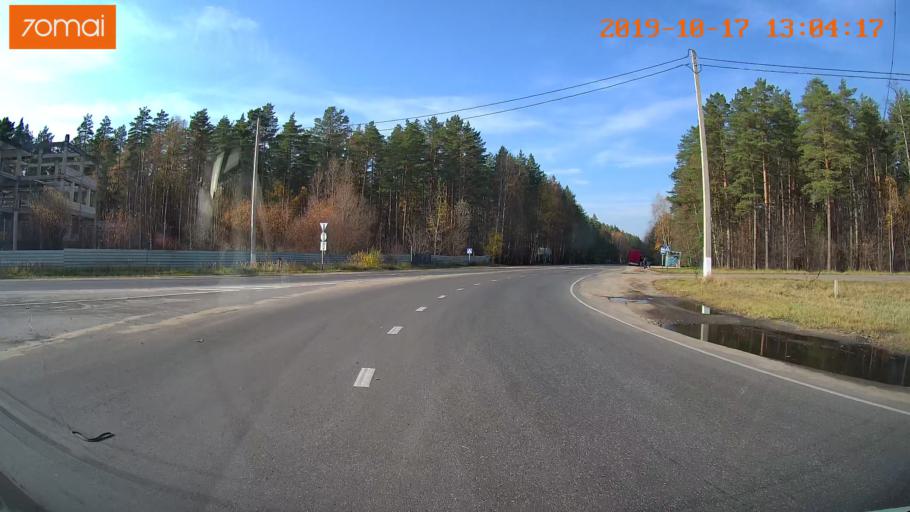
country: RU
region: Rjazan
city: Kasimov
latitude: 54.9608
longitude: 41.3454
